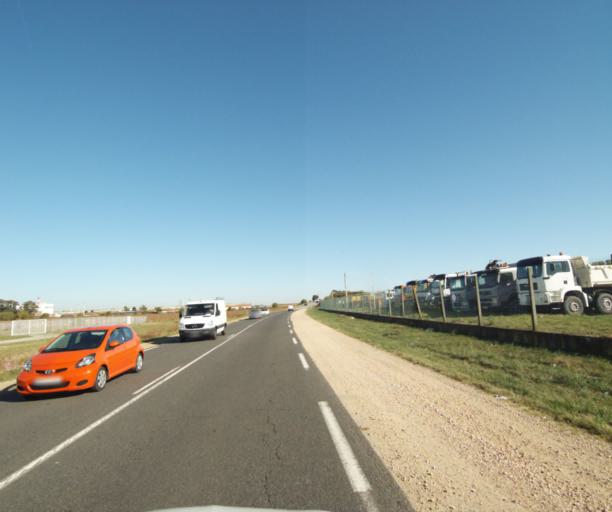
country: FR
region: Auvergne
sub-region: Departement du Puy-de-Dome
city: Aulnat
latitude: 45.8018
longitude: 3.1478
